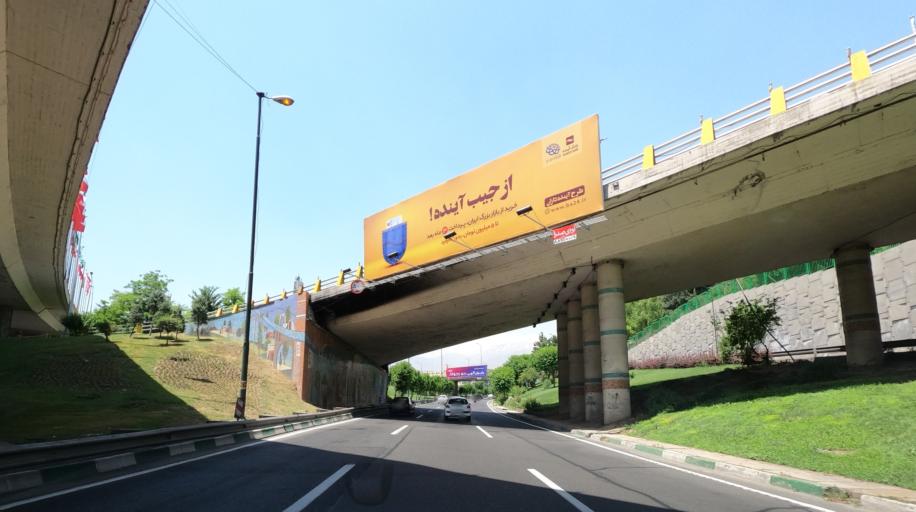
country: IR
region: Tehran
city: Tajrish
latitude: 35.7498
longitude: 51.4216
